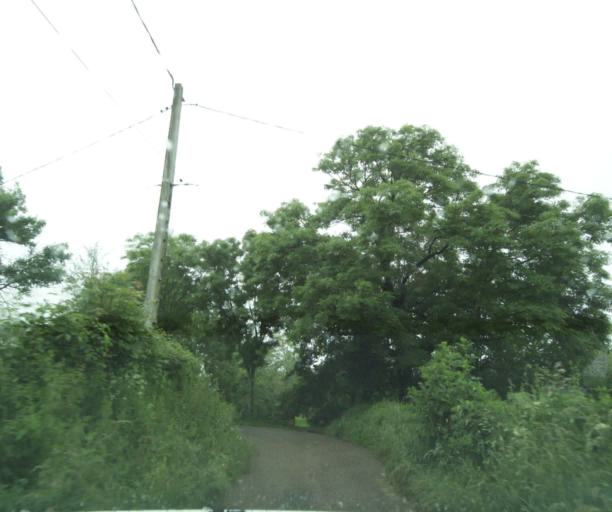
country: FR
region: Bourgogne
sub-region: Departement de Saone-et-Loire
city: La Clayette
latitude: 46.3697
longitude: 4.3505
